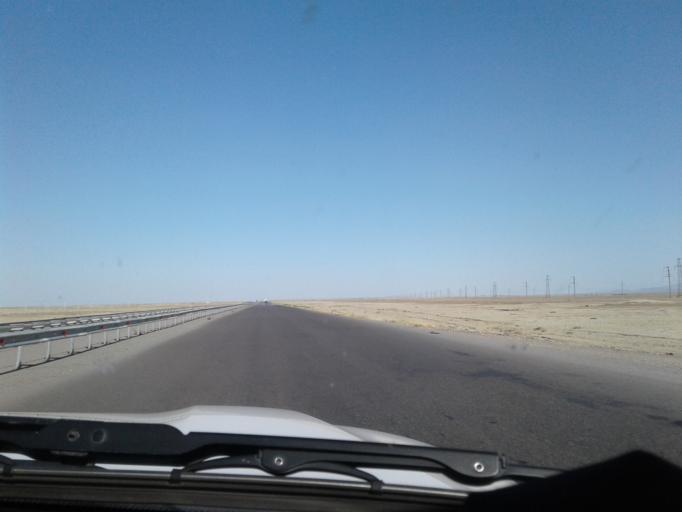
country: TM
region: Ahal
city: Kaka
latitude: 37.2681
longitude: 59.8284
